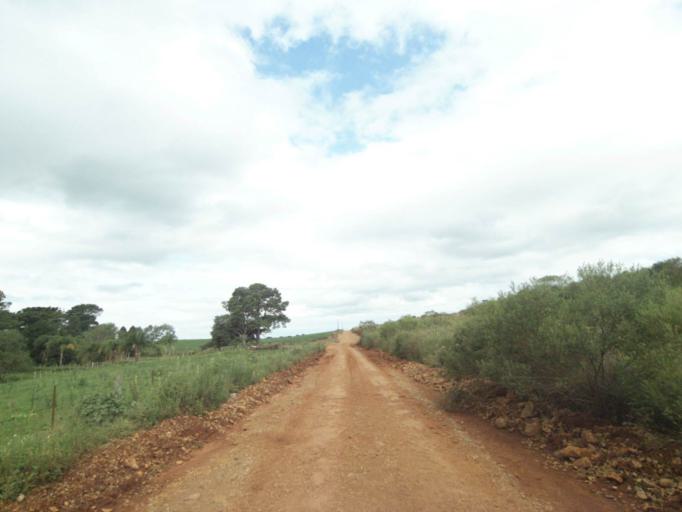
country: BR
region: Rio Grande do Sul
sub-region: Lagoa Vermelha
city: Lagoa Vermelha
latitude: -28.2018
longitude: -51.5175
